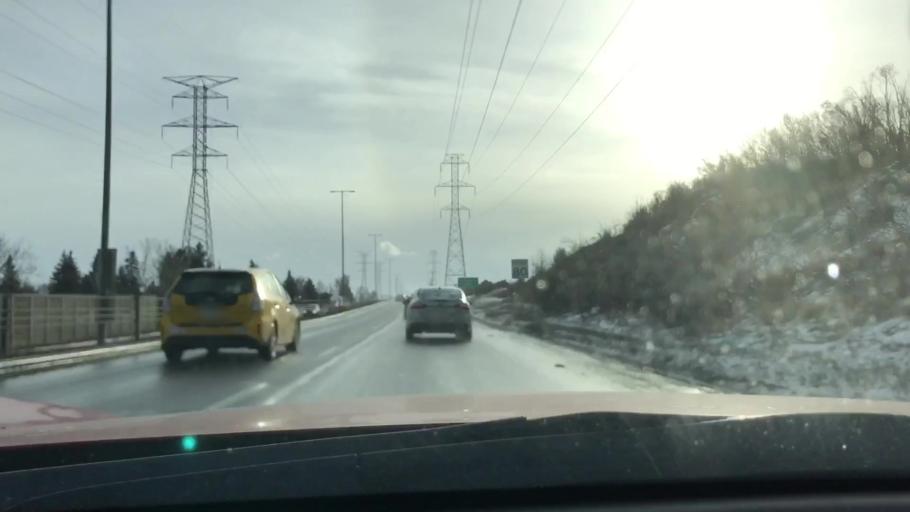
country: CA
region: Alberta
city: Calgary
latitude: 51.0498
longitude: -114.1643
